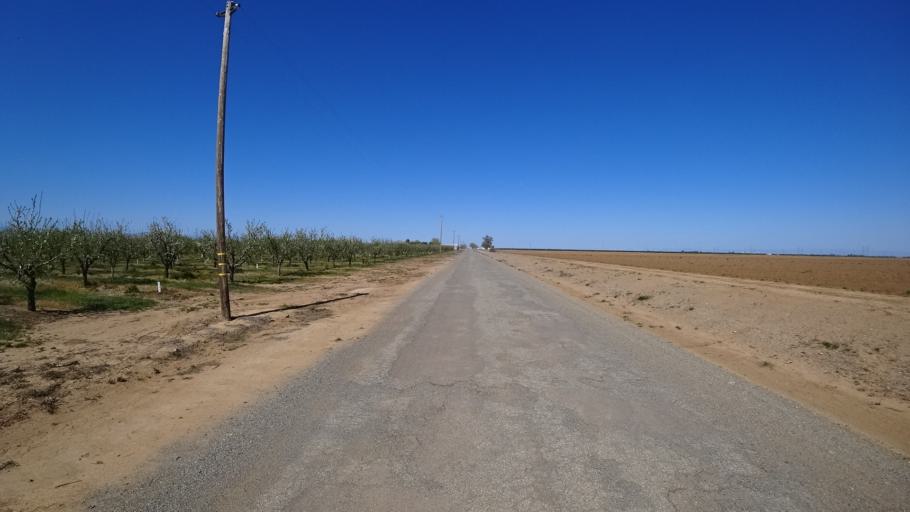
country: US
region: California
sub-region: Glenn County
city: Willows
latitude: 39.4809
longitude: -122.2772
